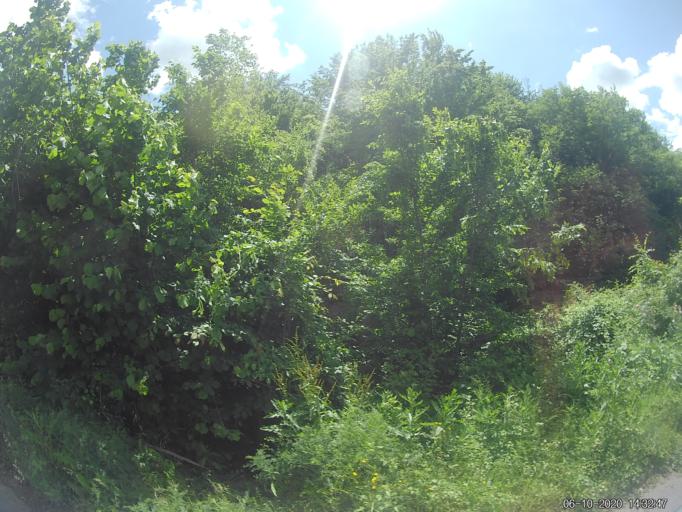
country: XK
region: Prizren
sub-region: Komuna e Therandes
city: Budakovo
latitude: 42.4152
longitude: 20.9264
